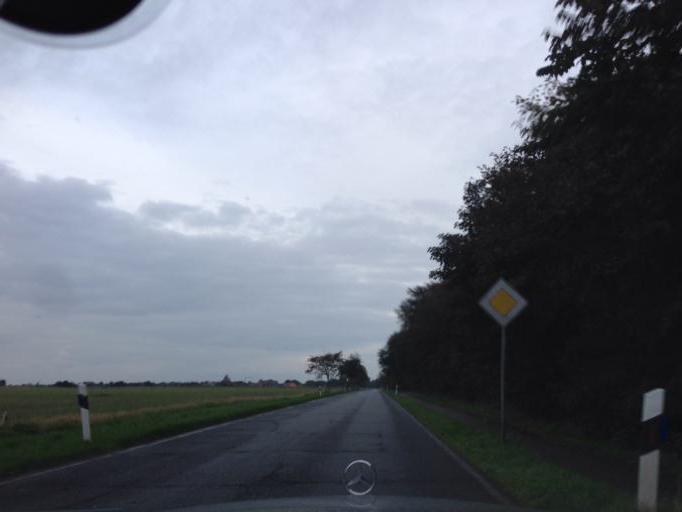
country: DE
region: Schleswig-Holstein
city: Oevenum
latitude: 54.6927
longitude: 8.5324
